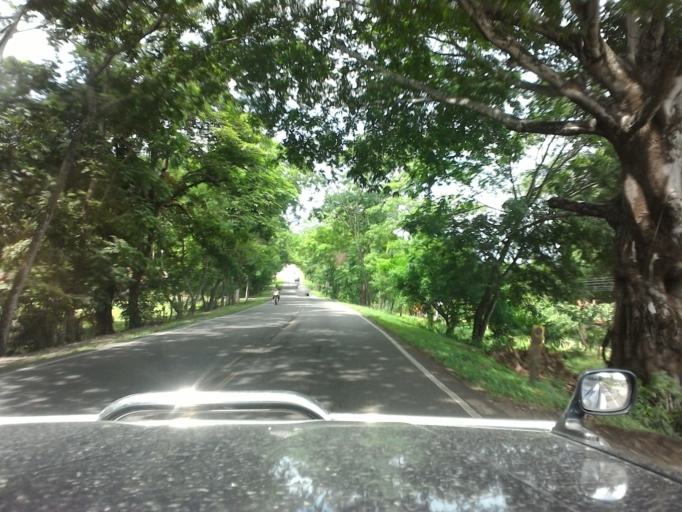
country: CR
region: Puntarenas
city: Esparza
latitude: 10.0111
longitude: -84.6184
